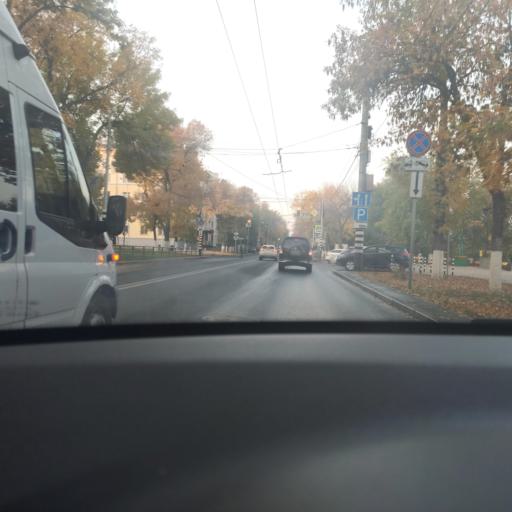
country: RU
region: Samara
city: Samara
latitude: 53.2107
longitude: 50.1200
